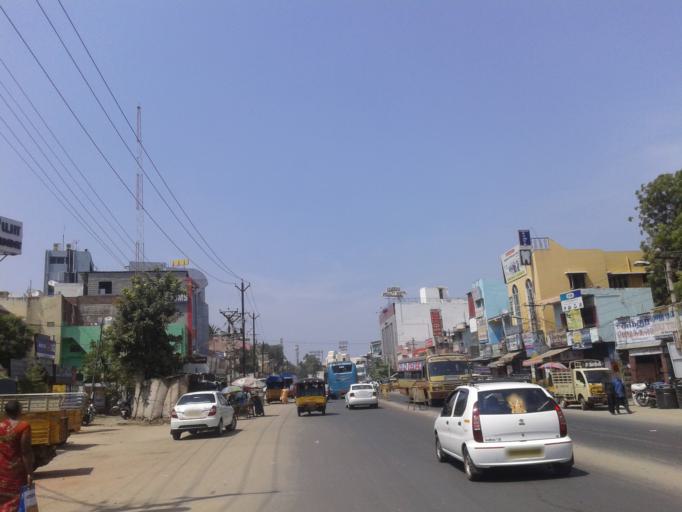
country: IN
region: Tamil Nadu
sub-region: Madurai
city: Madurai
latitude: 9.9322
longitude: 78.0934
